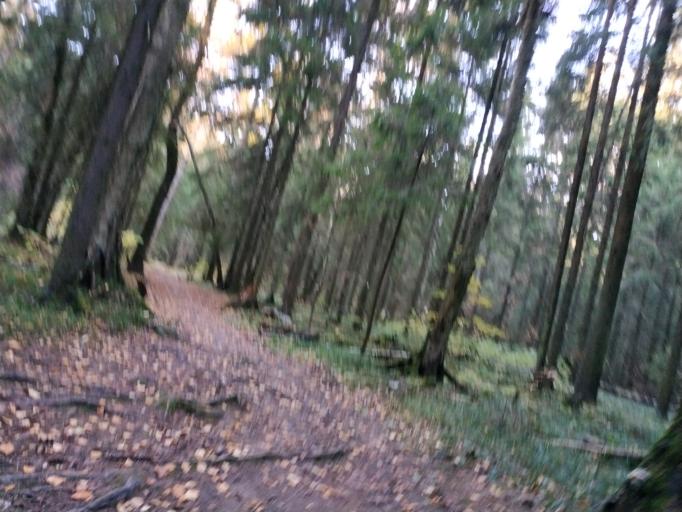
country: RU
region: Moskovskaya
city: Lobnya
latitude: 55.9949
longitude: 37.4682
